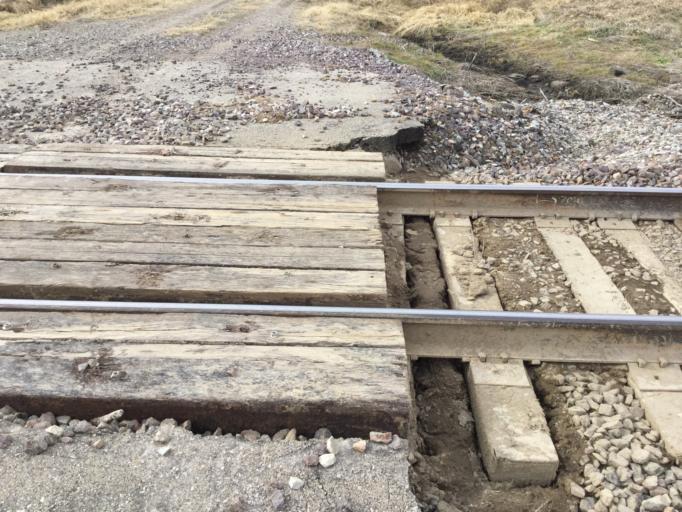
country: US
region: Kansas
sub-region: Marion County
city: Peabody
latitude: 38.0728
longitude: -97.1252
